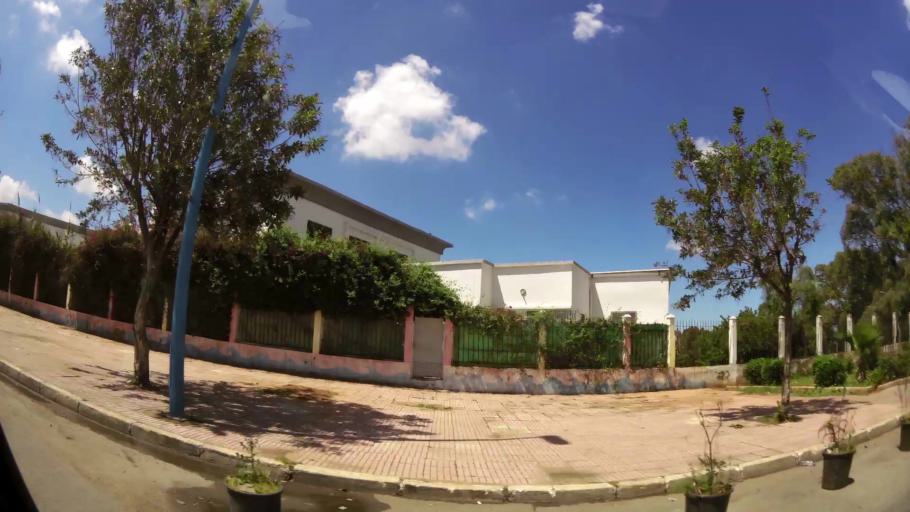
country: MA
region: Grand Casablanca
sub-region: Casablanca
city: Casablanca
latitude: 33.5636
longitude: -7.5758
